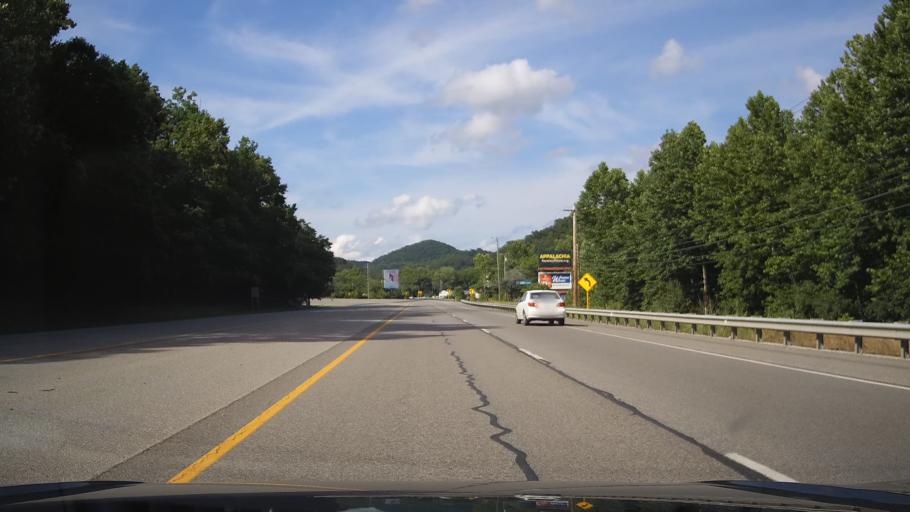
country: US
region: Kentucky
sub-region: Lawrence County
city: Louisa
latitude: 37.9698
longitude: -82.6697
